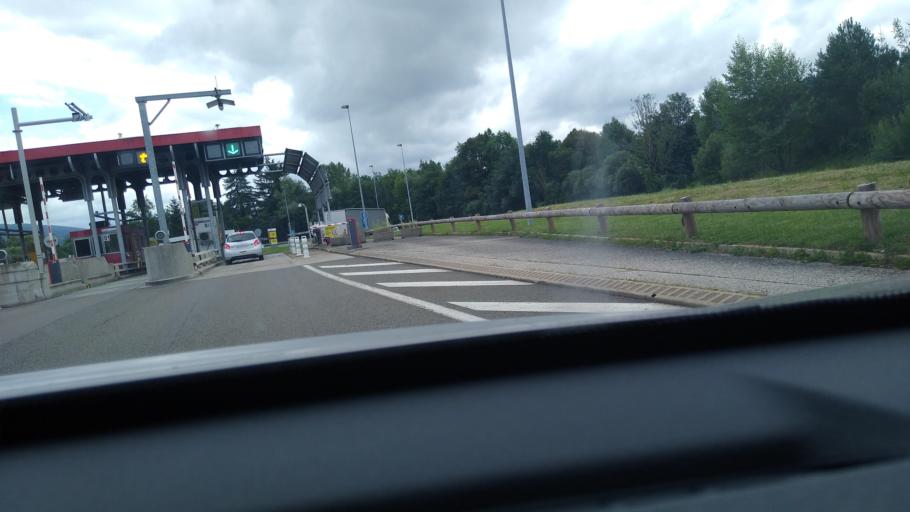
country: FR
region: Rhone-Alpes
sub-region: Departement de l'Ain
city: Saint-Martin-du-Frene
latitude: 46.1328
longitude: 5.5415
